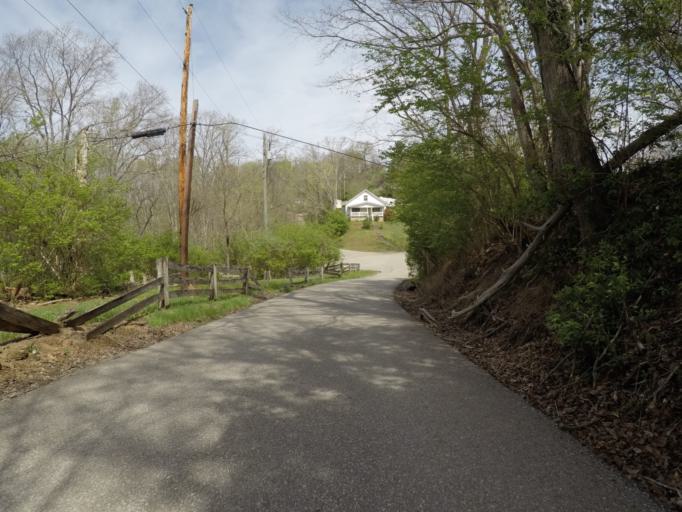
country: US
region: West Virginia
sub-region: Wayne County
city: Lavalette
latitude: 38.3442
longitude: -82.3748
